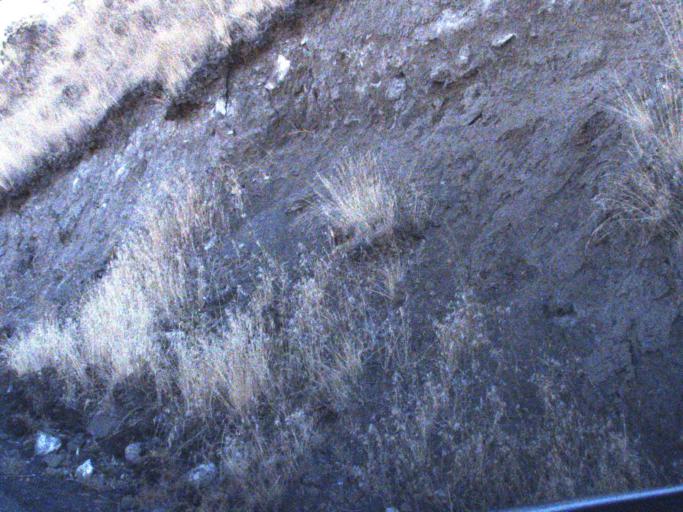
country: US
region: Washington
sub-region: Walla Walla County
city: Waitsburg
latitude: 46.6704
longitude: -118.3131
